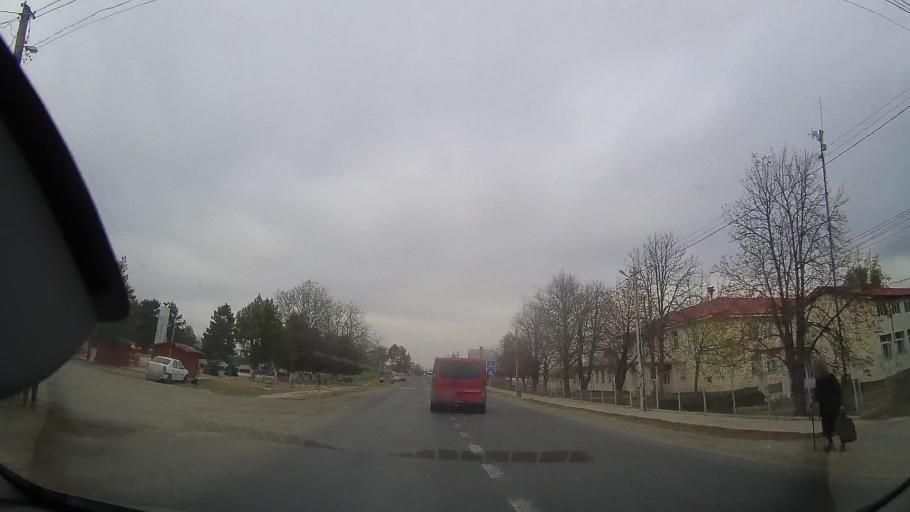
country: RO
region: Buzau
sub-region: Comuna Padina
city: Padina
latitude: 44.8287
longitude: 27.1128
